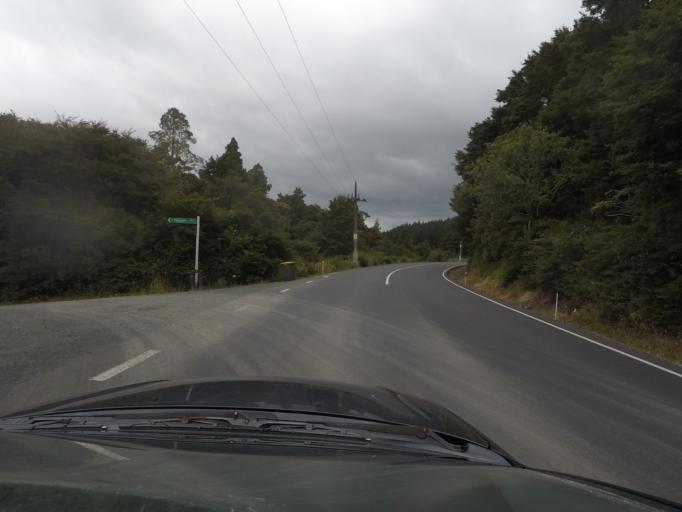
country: NZ
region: Auckland
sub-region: Auckland
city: Wellsford
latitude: -36.2858
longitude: 174.6130
